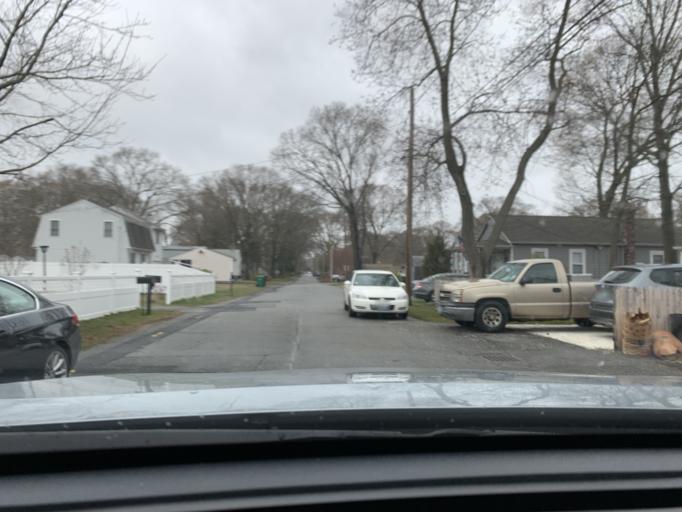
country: US
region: Rhode Island
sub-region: Kent County
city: Warwick
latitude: 41.6976
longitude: -71.4021
